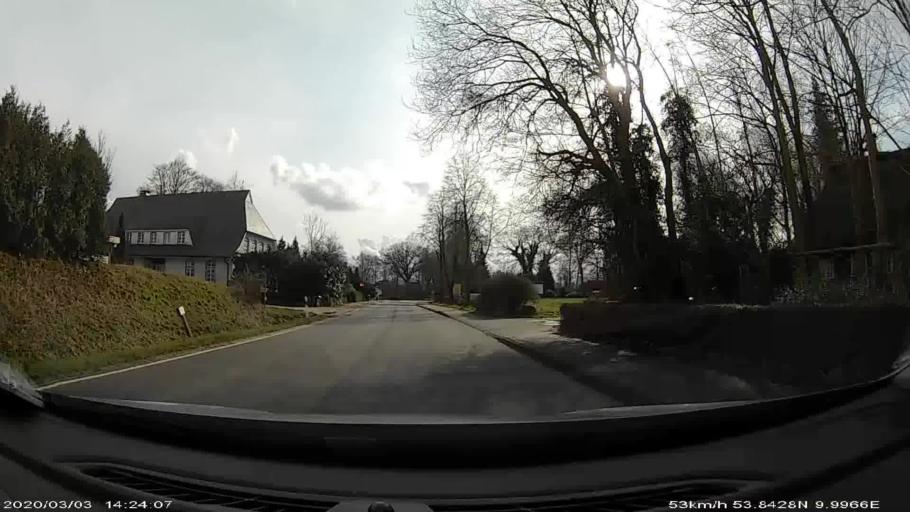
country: DE
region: Schleswig-Holstein
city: Oersdorf
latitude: 53.8427
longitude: 9.9965
